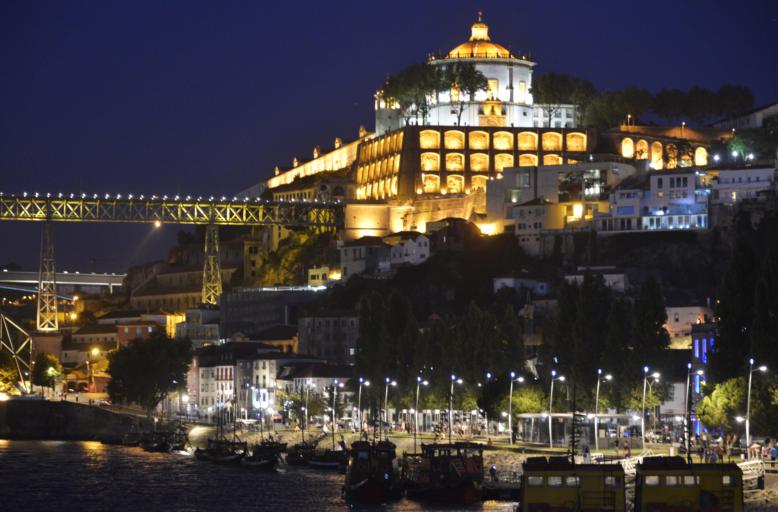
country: PT
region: Porto
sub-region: Vila Nova de Gaia
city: Vila Nova de Gaia
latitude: 41.1378
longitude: -8.6172
